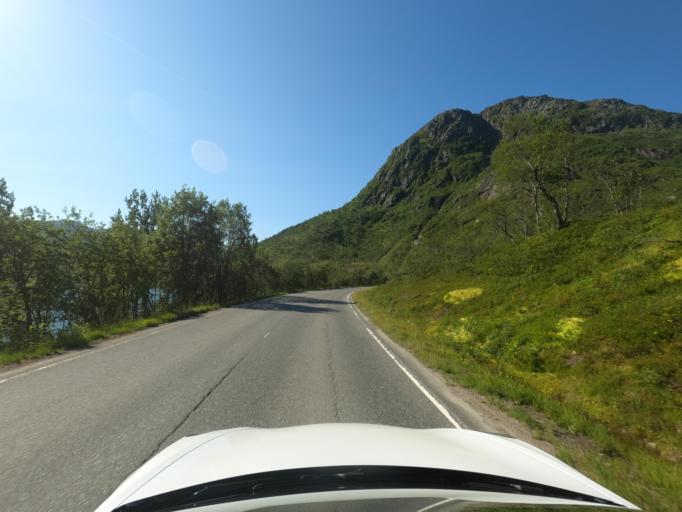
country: NO
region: Nordland
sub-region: Lodingen
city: Lodingen
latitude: 68.5588
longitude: 15.7501
